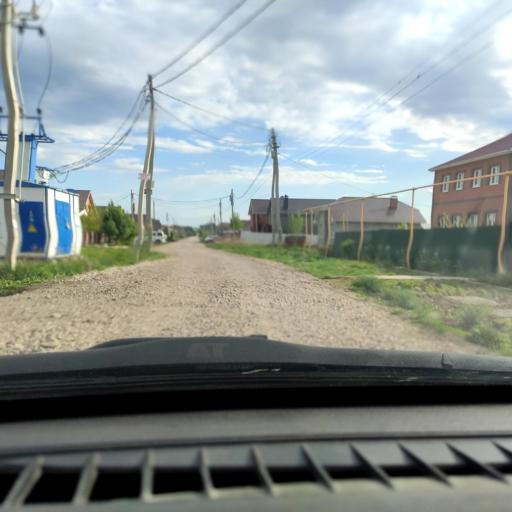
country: RU
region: Samara
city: Tol'yatti
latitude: 53.5661
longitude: 49.4077
